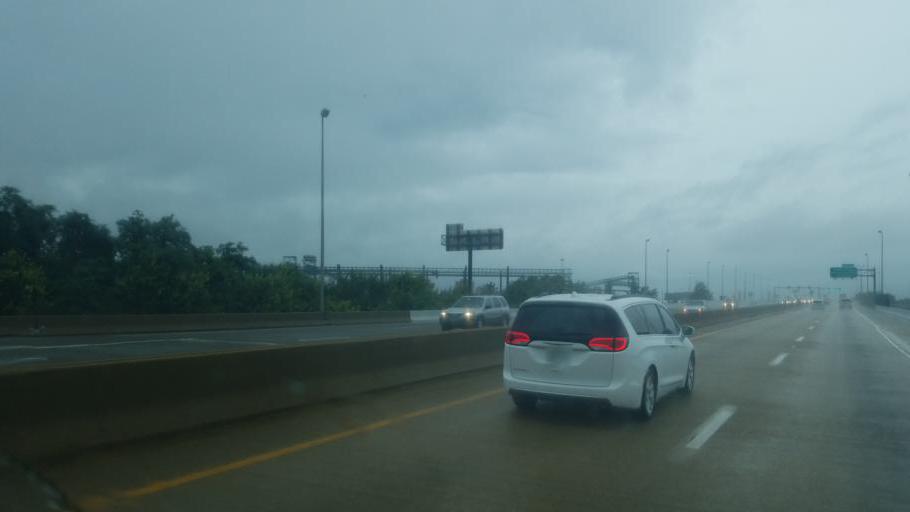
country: US
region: Virginia
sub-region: City of Newport News
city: Newport News
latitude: 36.9693
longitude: -76.4166
